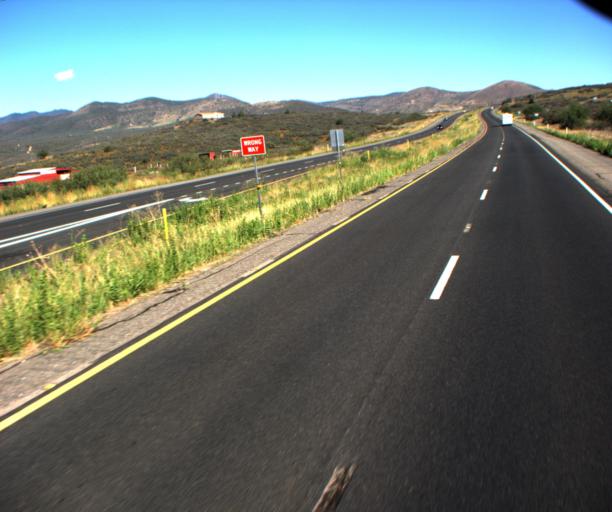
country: US
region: Arizona
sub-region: Yavapai County
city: Mayer
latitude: 34.4296
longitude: -112.2560
